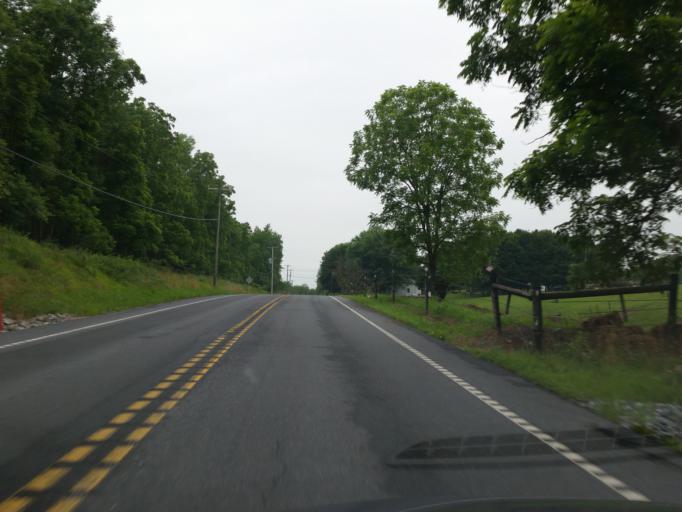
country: US
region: Pennsylvania
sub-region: Schuylkill County
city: Tower City
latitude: 40.5100
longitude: -76.5180
